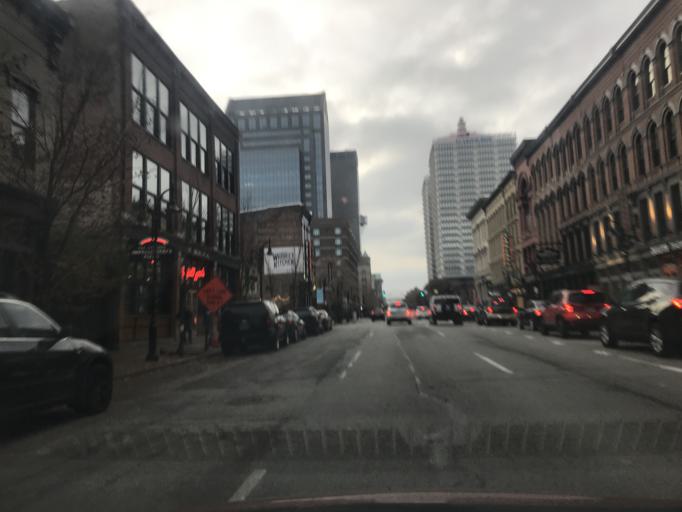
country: US
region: Kentucky
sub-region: Jefferson County
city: Louisville
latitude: 38.2561
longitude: -85.7519
